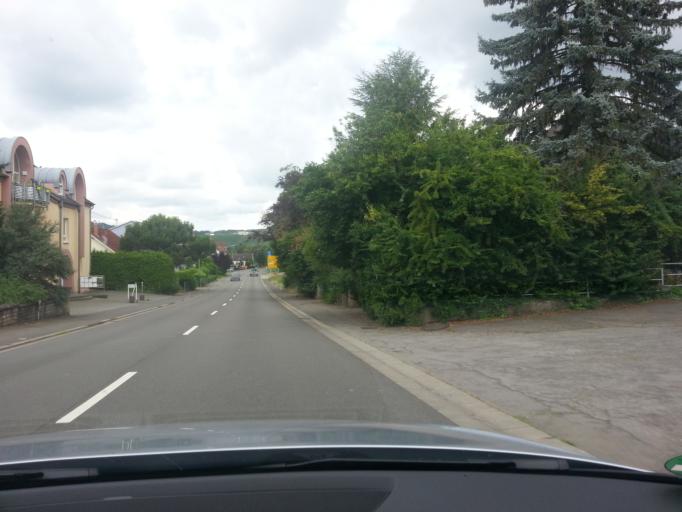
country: LU
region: Grevenmacher
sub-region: Canton de Remich
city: Remich
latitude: 49.5401
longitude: 6.3814
